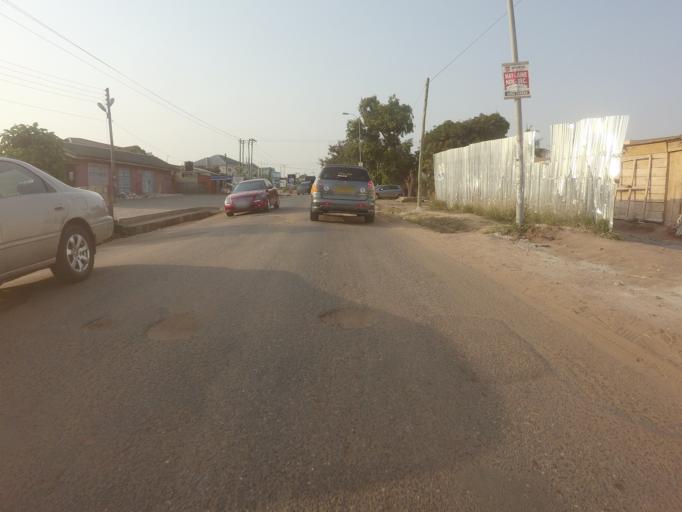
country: GH
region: Greater Accra
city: Nungua
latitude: 5.6170
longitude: -0.0525
